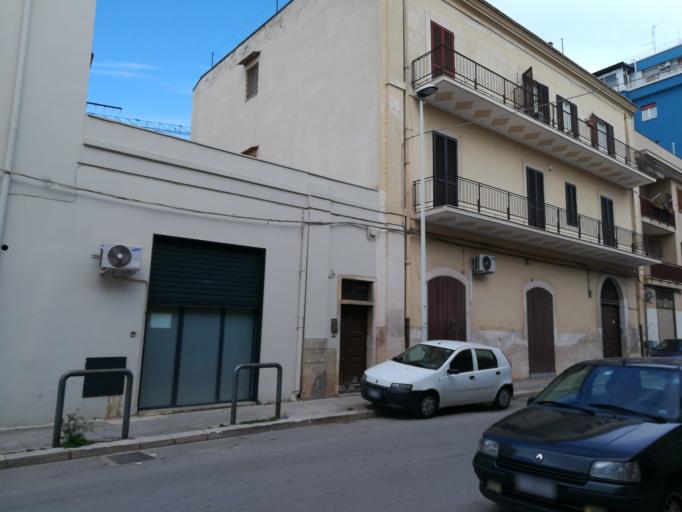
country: IT
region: Apulia
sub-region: Provincia di Bari
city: Bitonto
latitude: 41.1071
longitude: 16.6860
